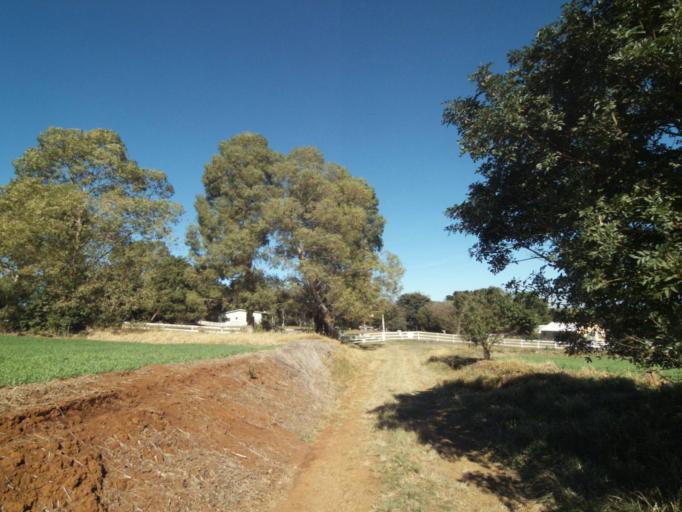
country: BR
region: Parana
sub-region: Tibagi
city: Tibagi
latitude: -24.5487
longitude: -50.2990
